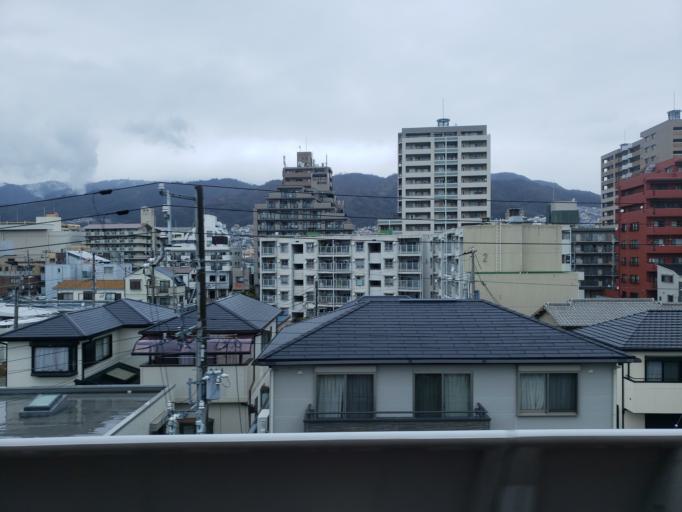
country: JP
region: Hyogo
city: Ashiya
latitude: 34.7224
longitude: 135.2907
